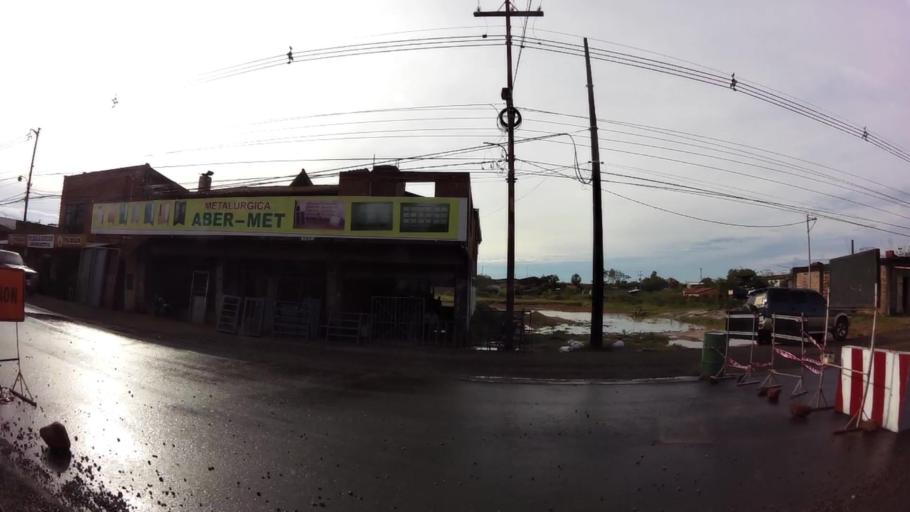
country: PY
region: Central
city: Limpio
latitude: -25.1787
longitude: -57.4875
